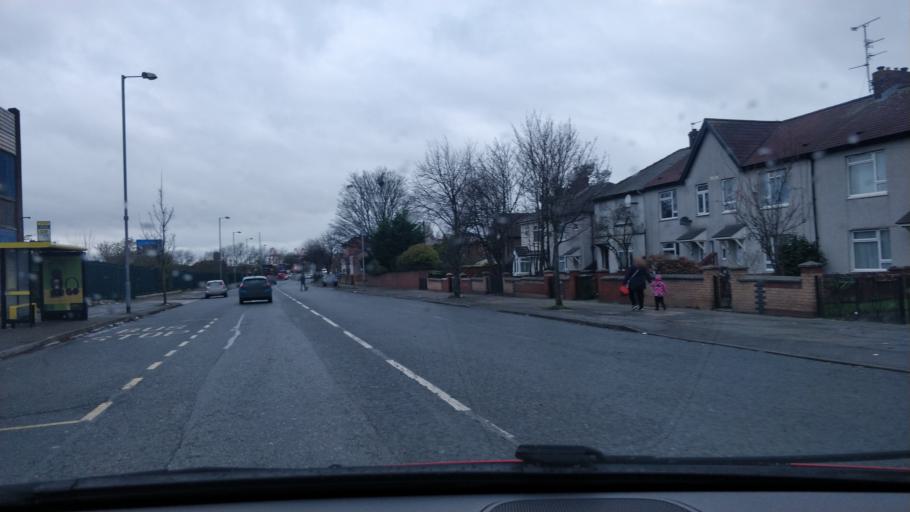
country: GB
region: England
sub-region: Sefton
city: Litherland
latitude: 53.4609
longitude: -2.9819
